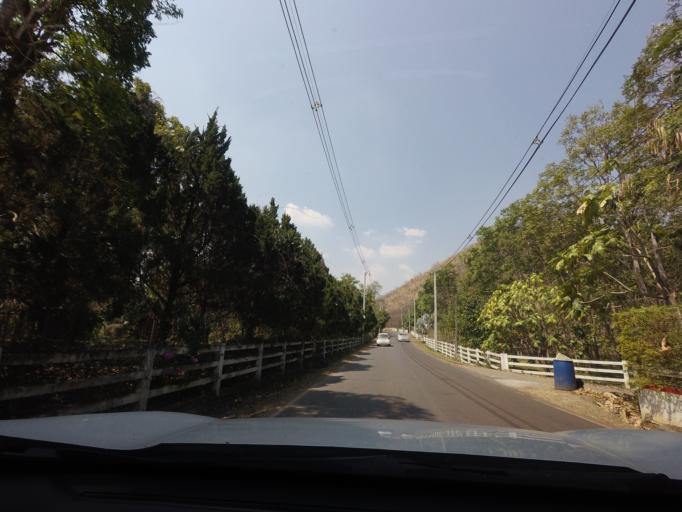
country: TH
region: Nakhon Ratchasima
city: Pak Chong
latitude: 14.5790
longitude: 101.4335
